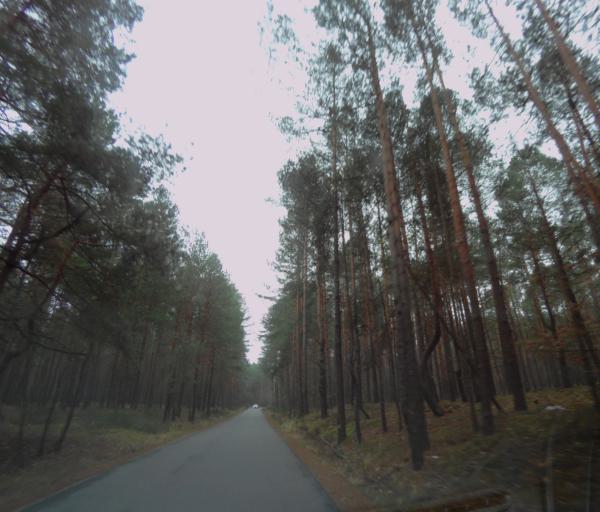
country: PL
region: Subcarpathian Voivodeship
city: Nowa Sarzyna
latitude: 50.3062
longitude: 22.3459
